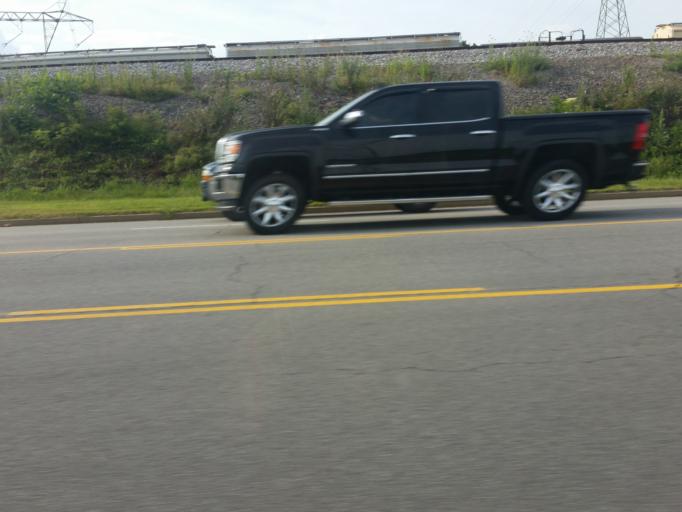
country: US
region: Tennessee
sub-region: Humphreys County
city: New Johnsonville
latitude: 36.0196
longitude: -87.9730
